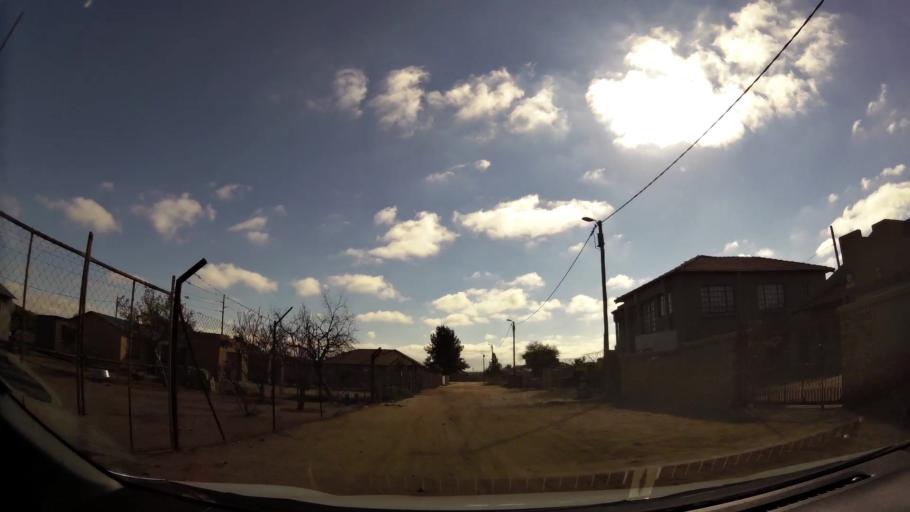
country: ZA
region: Limpopo
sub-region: Capricorn District Municipality
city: Polokwane
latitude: -23.8453
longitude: 29.4023
